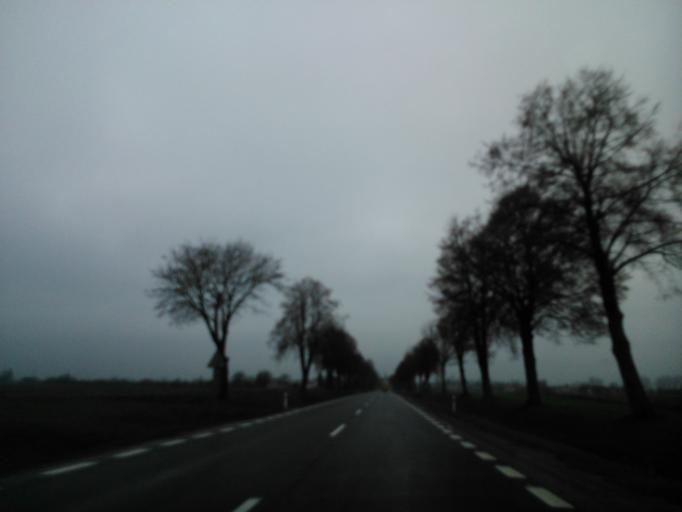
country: PL
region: Swietokrzyskie
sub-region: Powiat opatowski
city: Wojciechowice
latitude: 50.8411
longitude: 21.6392
